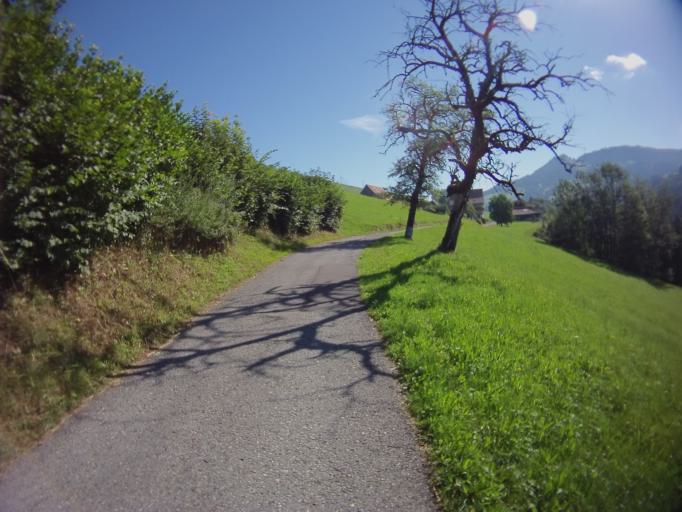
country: CH
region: Schwyz
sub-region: Bezirk Schwyz
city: Sattel
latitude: 47.0883
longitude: 8.6506
